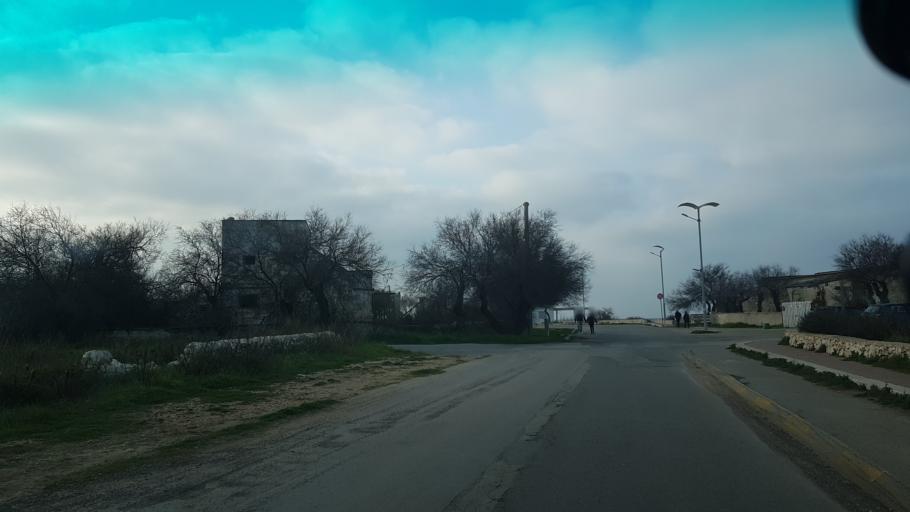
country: IT
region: Apulia
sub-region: Provincia di Brindisi
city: Carovigno
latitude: 40.7439
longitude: 17.7351
